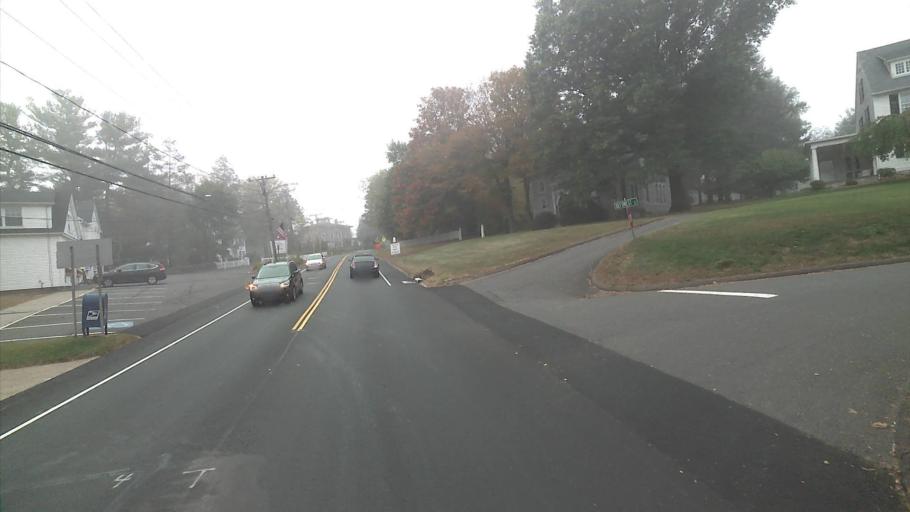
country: US
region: Connecticut
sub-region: Litchfield County
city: Watertown
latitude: 41.6054
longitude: -73.1190
